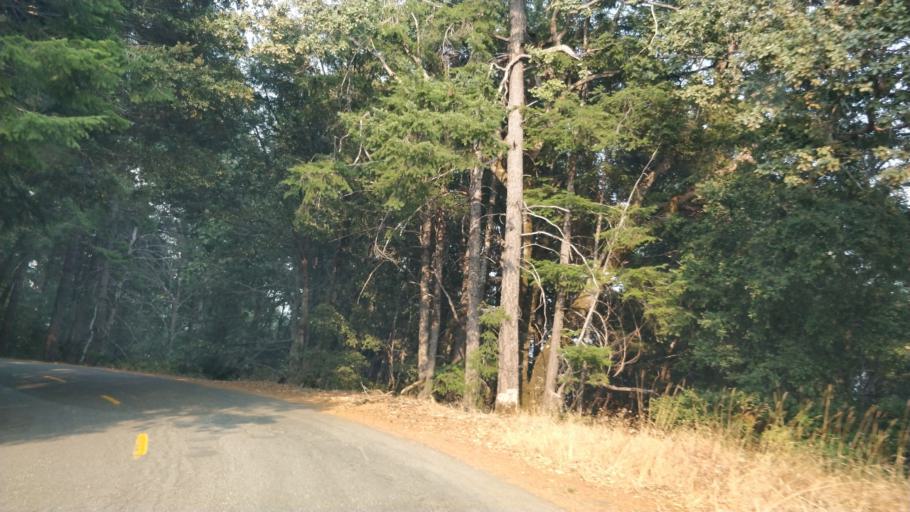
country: US
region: California
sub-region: Humboldt County
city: Rio Dell
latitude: 40.2678
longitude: -124.0770
